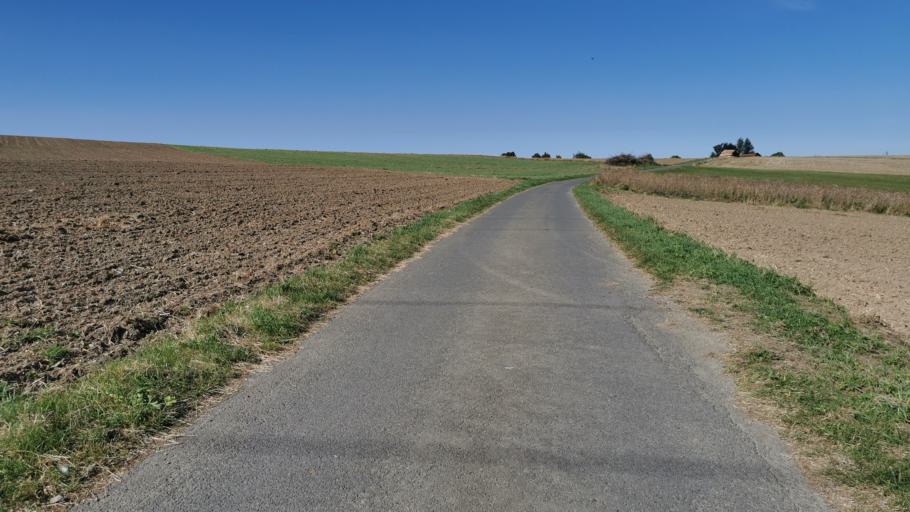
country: DE
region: Bavaria
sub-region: Upper Franconia
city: Ludwigsstadt
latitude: 50.4551
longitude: 11.4104
